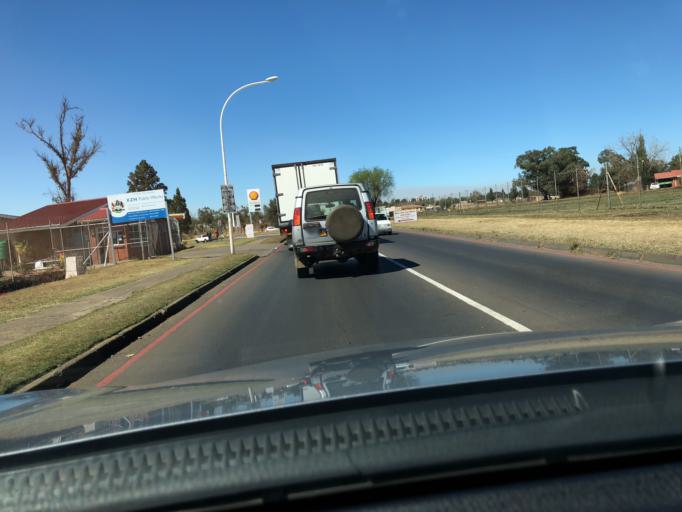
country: ZA
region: KwaZulu-Natal
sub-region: Amajuba District Municipality
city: Newcastle
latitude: -27.7596
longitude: 29.9449
